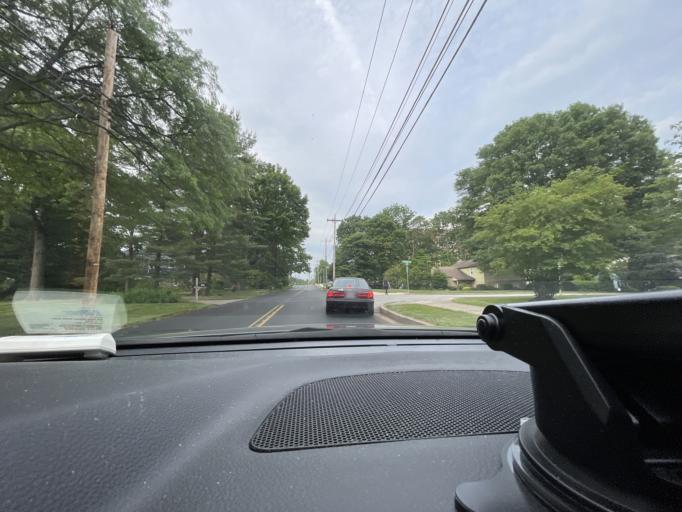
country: US
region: Pennsylvania
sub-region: Montgomery County
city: Plymouth Meeting
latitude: 40.1210
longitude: -75.2924
